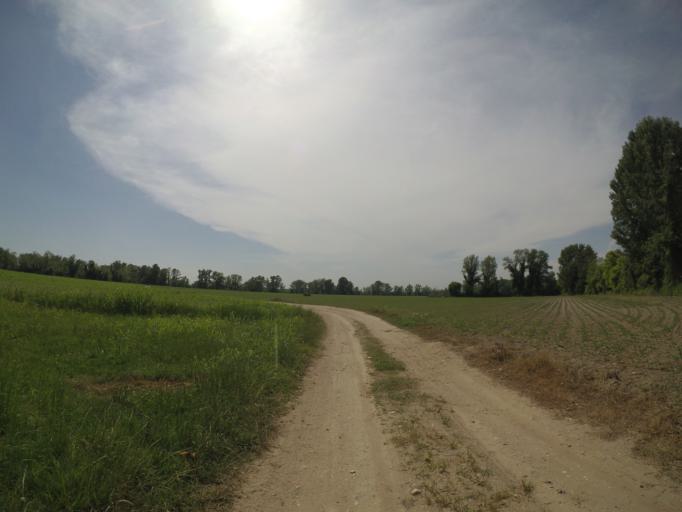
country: IT
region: Friuli Venezia Giulia
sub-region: Provincia di Udine
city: Camino al Tagliamento
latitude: 45.9134
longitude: 12.9260
